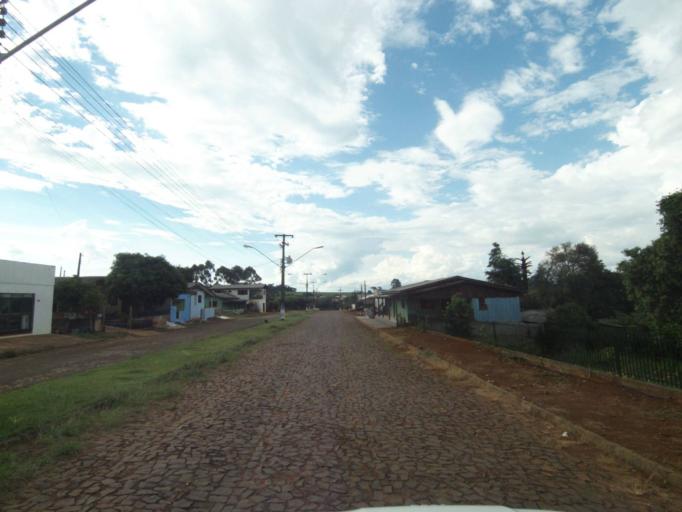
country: BR
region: Parana
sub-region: Laranjeiras Do Sul
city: Laranjeiras do Sul
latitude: -25.4914
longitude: -52.5300
